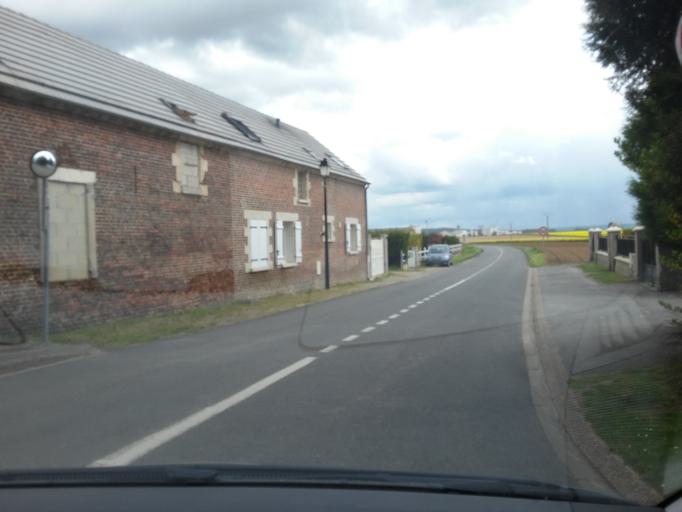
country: FR
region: Picardie
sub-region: Departement de l'Oise
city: Grandfresnoy
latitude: 49.3640
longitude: 2.6429
